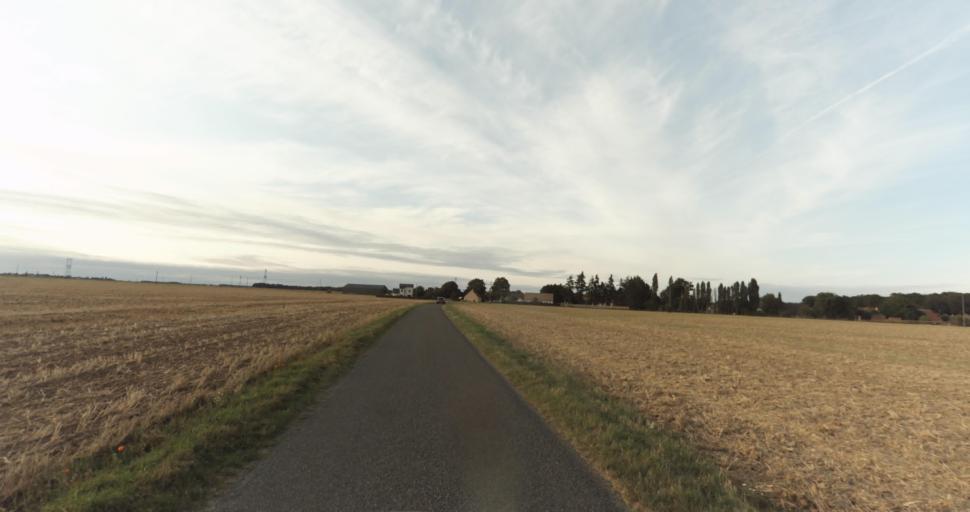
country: FR
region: Haute-Normandie
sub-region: Departement de l'Eure
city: Marcilly-sur-Eure
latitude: 48.8443
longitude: 1.2727
